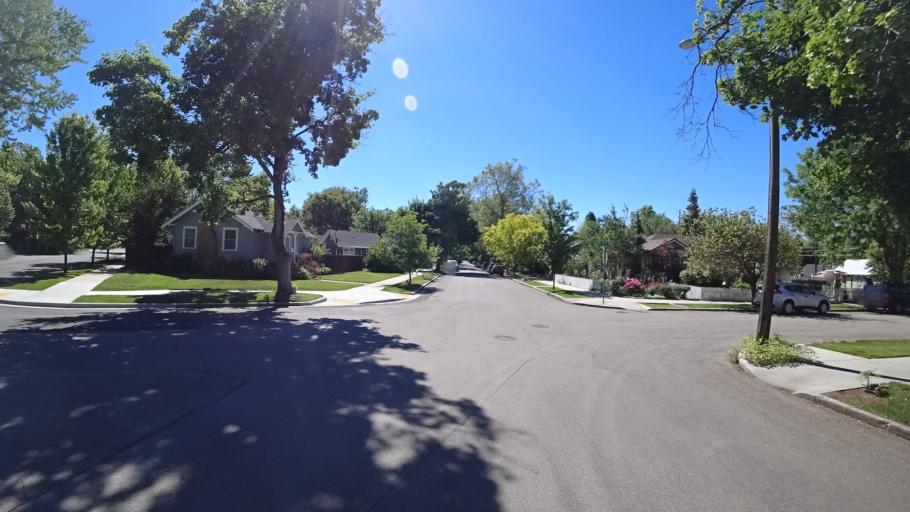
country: US
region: Idaho
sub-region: Ada County
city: Boise
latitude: 43.6291
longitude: -116.2170
